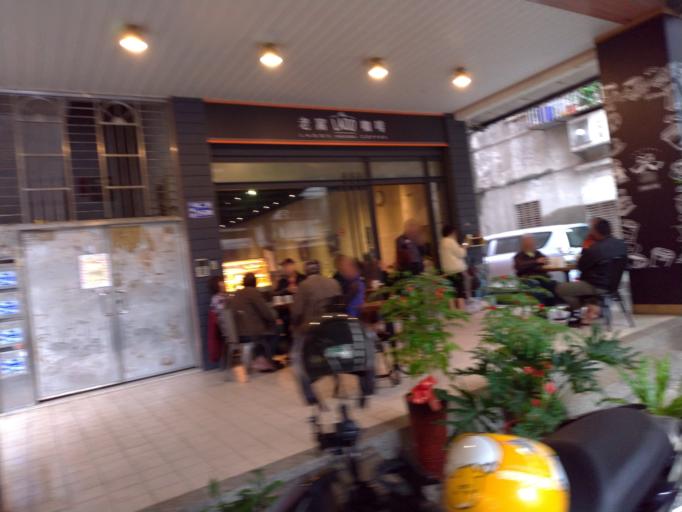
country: TW
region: Taiwan
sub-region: Keelung
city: Keelung
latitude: 25.0834
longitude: 121.6961
